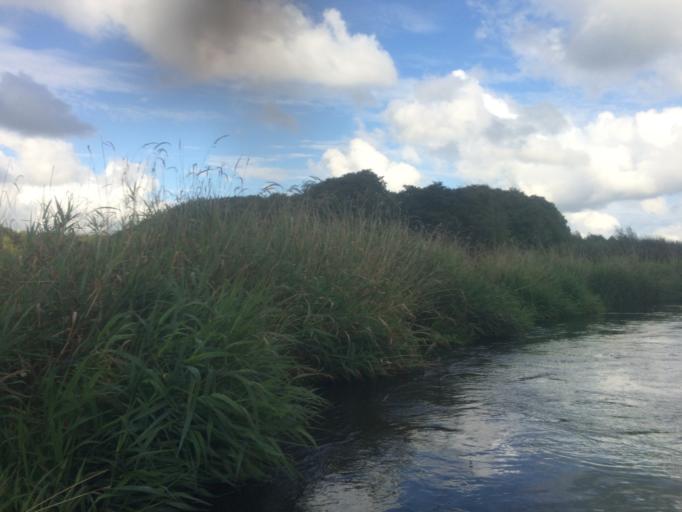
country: DK
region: South Denmark
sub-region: Vejle Kommune
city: Egtved
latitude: 55.6628
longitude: 9.3204
